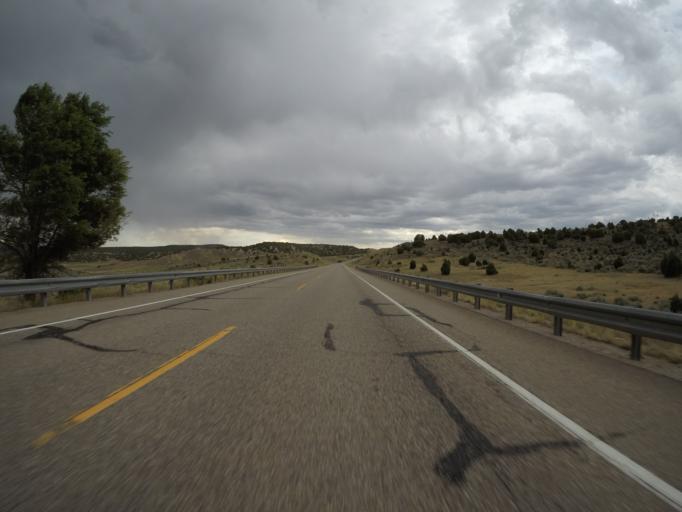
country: US
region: Colorado
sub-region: Rio Blanco County
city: Rangely
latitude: 40.3658
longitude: -108.4137
